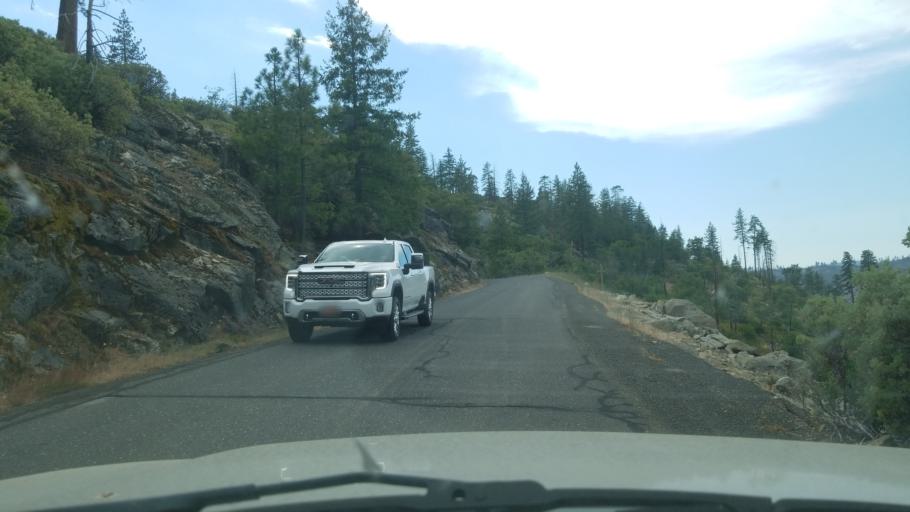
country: US
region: California
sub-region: Mariposa County
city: Yosemite Valley
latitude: 37.9032
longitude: -119.8235
